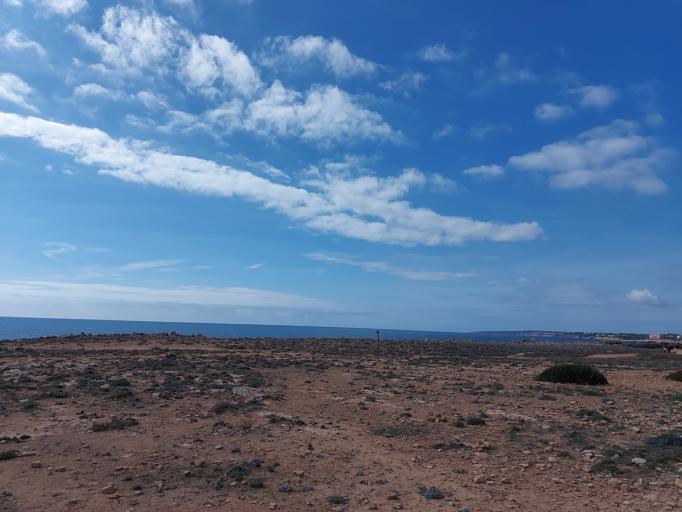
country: ES
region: Balearic Islands
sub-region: Illes Balears
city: Llucmajor
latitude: 39.3588
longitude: 2.9021
